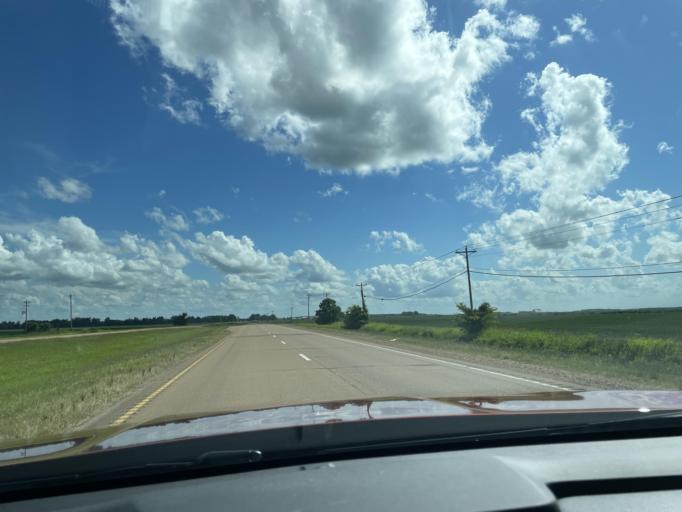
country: US
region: Mississippi
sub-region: Humphreys County
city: Belzoni
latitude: 33.1528
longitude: -90.5061
